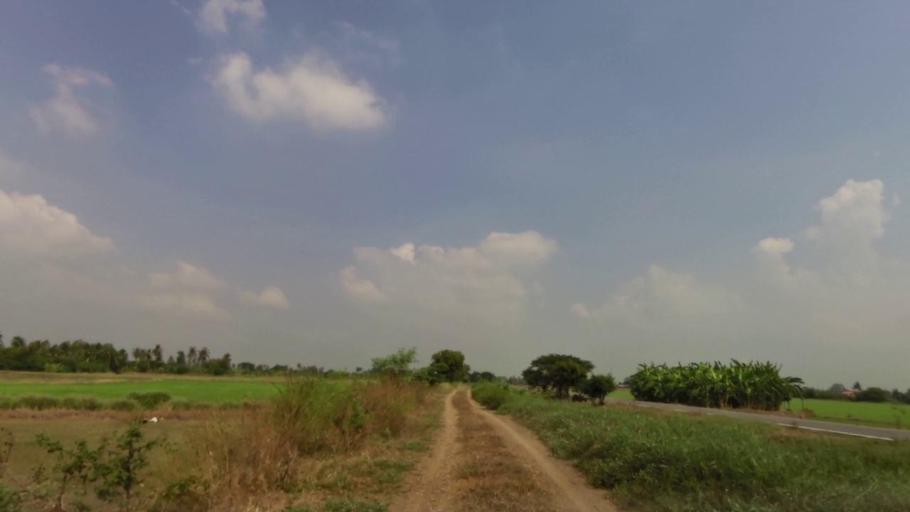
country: TH
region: Ang Thong
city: Pho Thong
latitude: 14.6238
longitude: 100.4043
